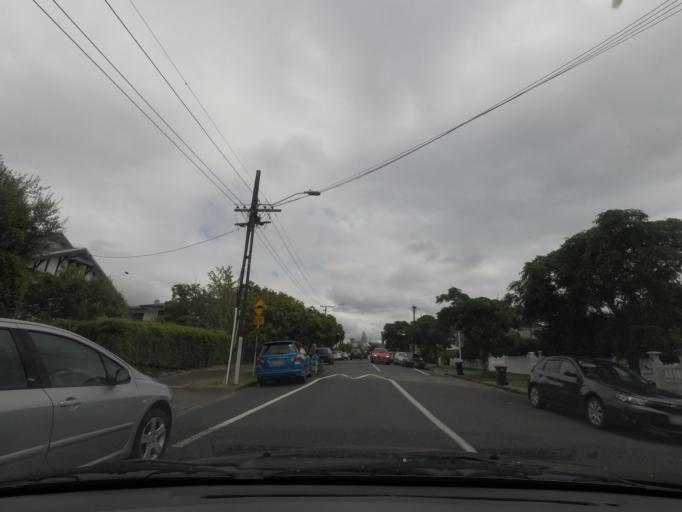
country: NZ
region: Auckland
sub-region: Auckland
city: Auckland
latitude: -36.8688
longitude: 174.7838
